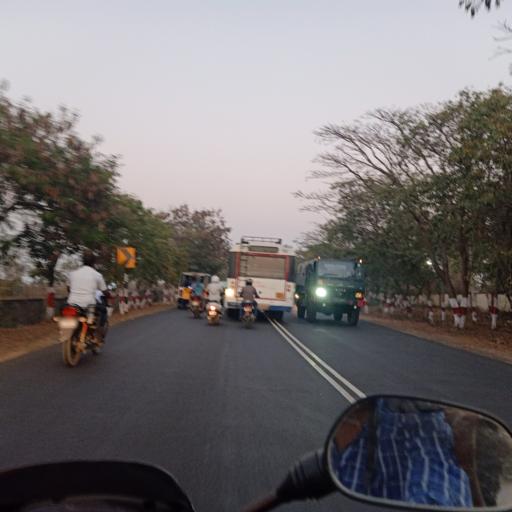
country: IN
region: Telangana
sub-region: Rangareddi
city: Secunderabad
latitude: 17.5424
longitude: 78.5296
